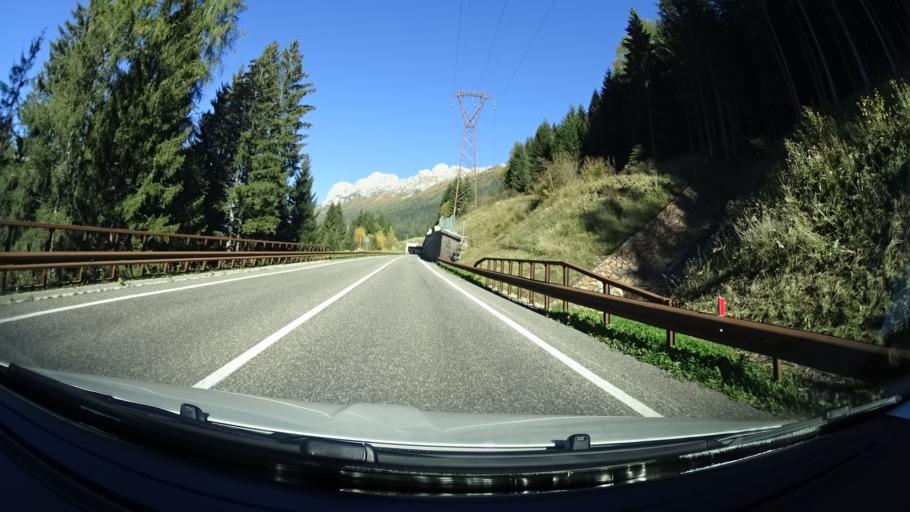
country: IT
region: Trentino-Alto Adige
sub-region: Provincia di Trento
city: Moena
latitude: 46.3694
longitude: 11.6553
